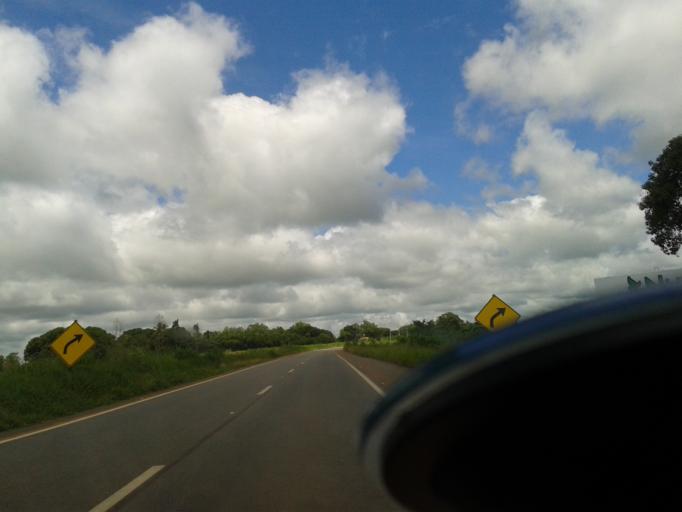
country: BR
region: Goias
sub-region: Itaberai
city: Itaberai
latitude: -16.0696
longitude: -49.7674
